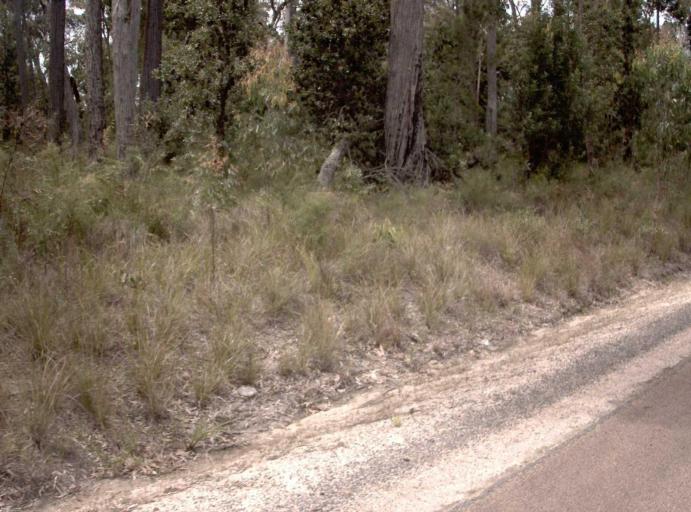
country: AU
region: New South Wales
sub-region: Bega Valley
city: Eden
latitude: -37.5035
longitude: 149.5350
